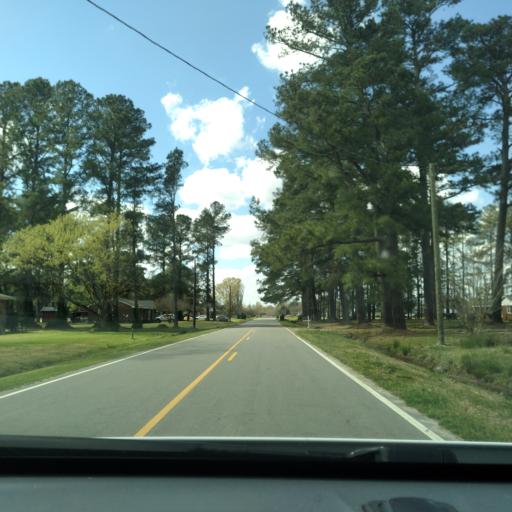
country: US
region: North Carolina
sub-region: Washington County
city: Plymouth
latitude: 35.8333
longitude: -76.7153
